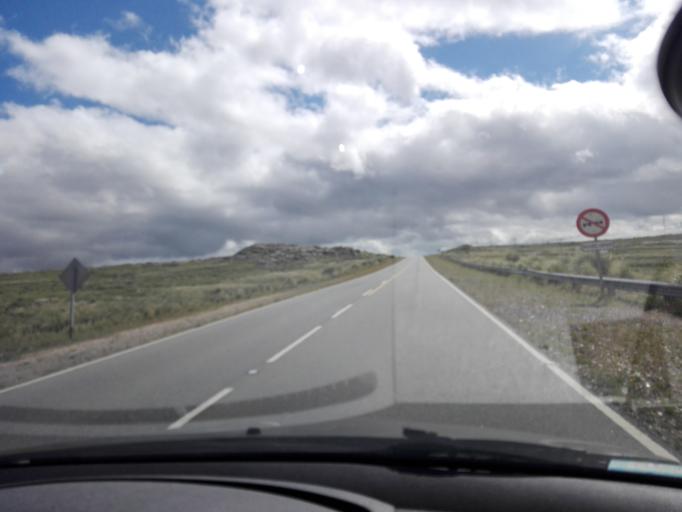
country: AR
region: Cordoba
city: Mina Clavero
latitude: -31.6141
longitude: -64.8459
